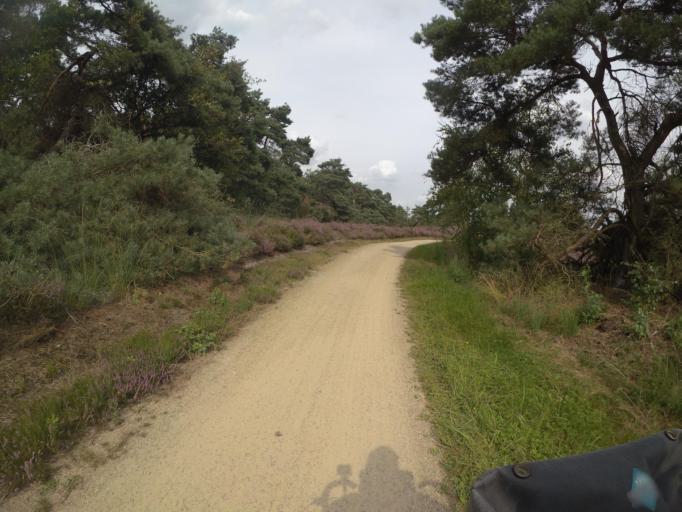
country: NL
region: Limburg
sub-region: Gemeente Bergen
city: Wellerlooi
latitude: 51.6128
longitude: 6.0785
